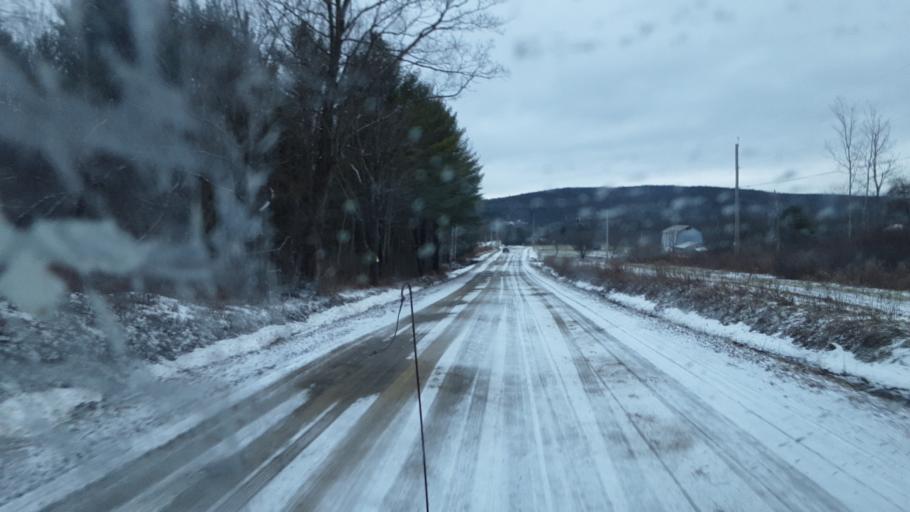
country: US
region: New York
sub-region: Allegany County
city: Friendship
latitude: 42.2912
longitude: -78.1623
